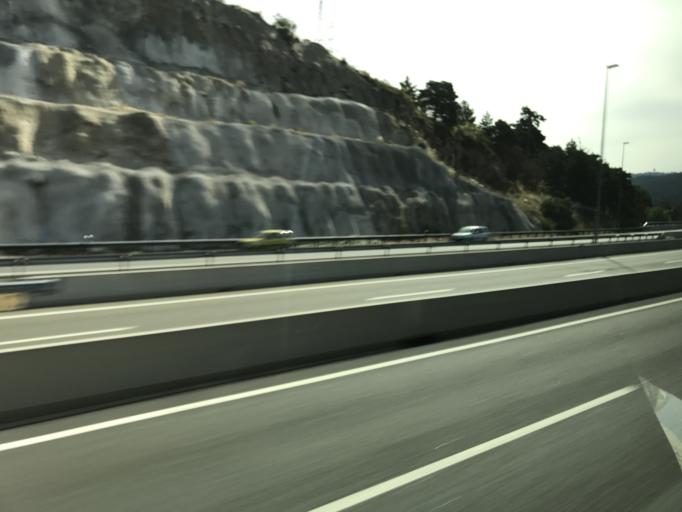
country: ES
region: Castille and Leon
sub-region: Provincia de Avila
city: Peguerinos
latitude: 40.7153
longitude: -4.1857
